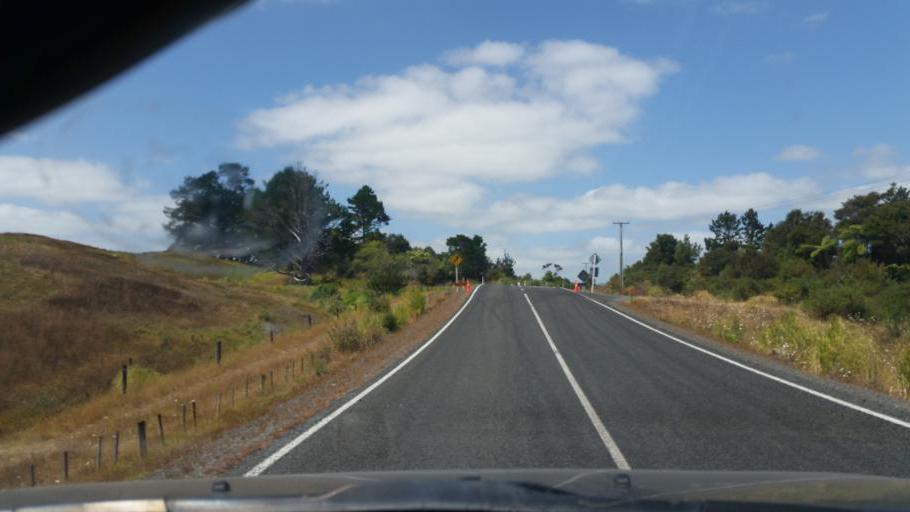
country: NZ
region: Northland
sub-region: Whangarei
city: Ruakaka
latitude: -36.0353
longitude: 174.2794
